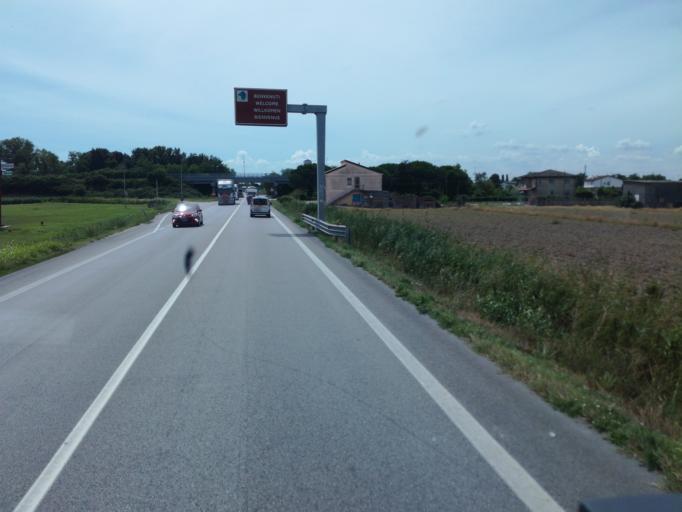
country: IT
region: Veneto
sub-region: Provincia di Rovigo
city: Rosolina
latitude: 45.1062
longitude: 12.2542
